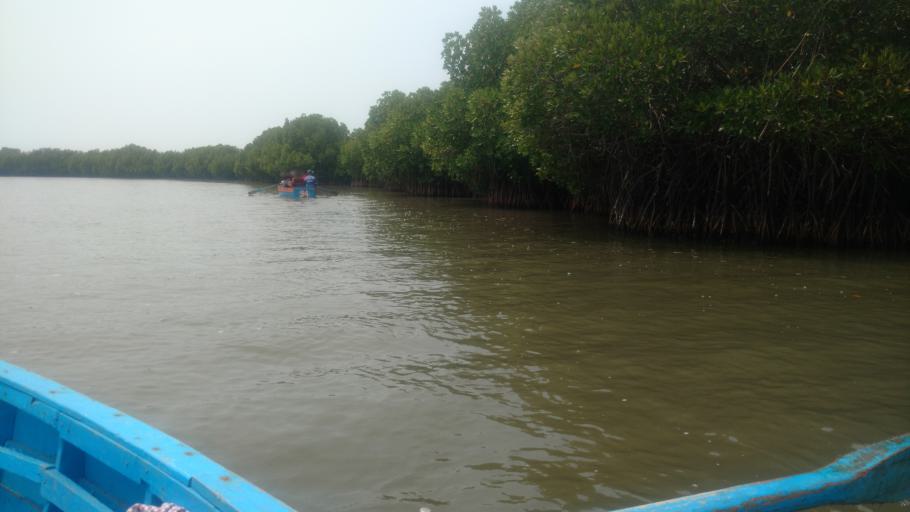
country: IN
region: Tamil Nadu
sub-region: Cuddalore
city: Annamalainagar
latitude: 11.4310
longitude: 79.7883
